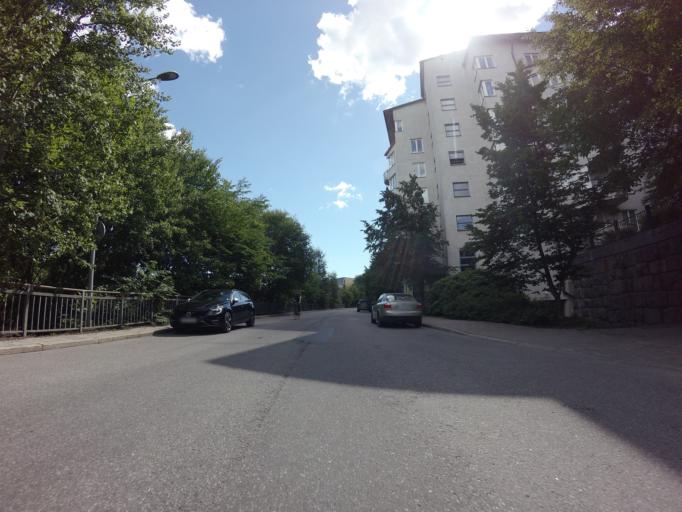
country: SE
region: Stockholm
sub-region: Stockholms Kommun
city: Stockholm
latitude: 59.3523
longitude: 18.0625
